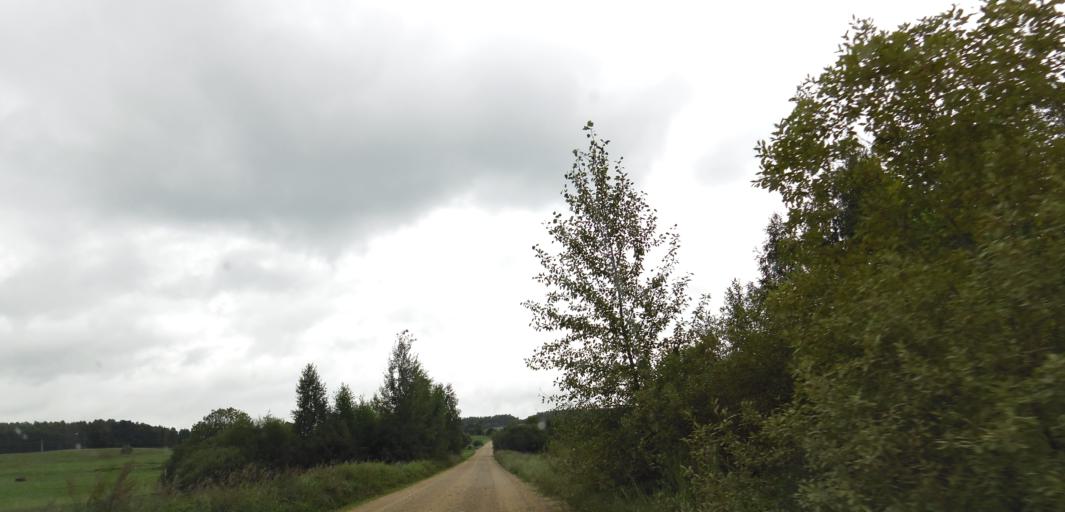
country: LT
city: Moletai
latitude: 55.3449
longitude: 25.3794
